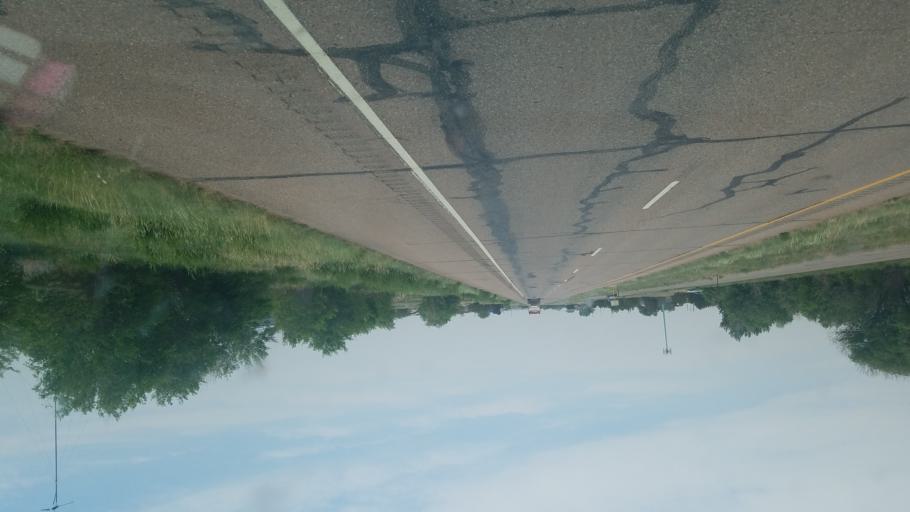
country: US
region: Colorado
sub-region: Fremont County
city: Penrose
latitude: 38.4059
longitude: -104.9934
